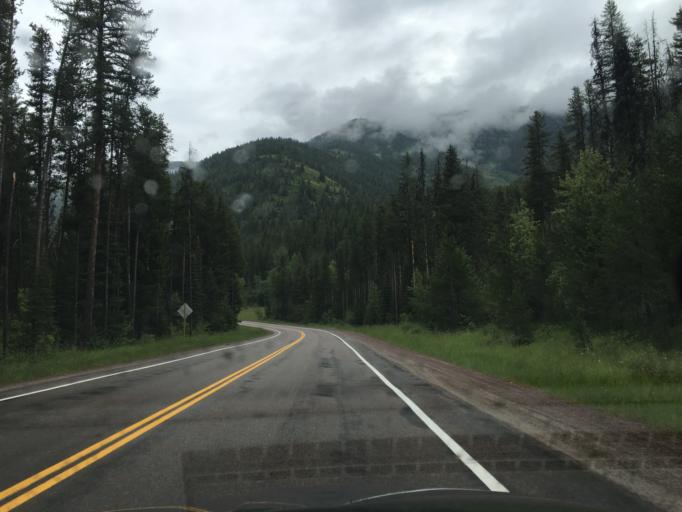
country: US
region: Montana
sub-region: Flathead County
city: Bigfork
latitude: 48.2410
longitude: -113.5677
